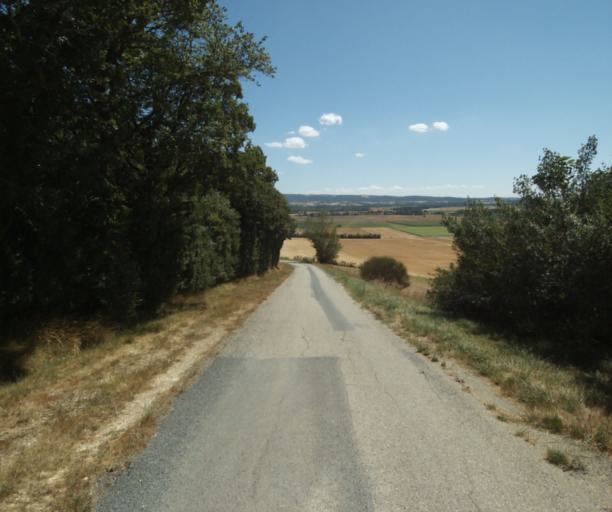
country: FR
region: Midi-Pyrenees
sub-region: Departement de la Haute-Garonne
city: Saint-Felix-Lauragais
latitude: 43.4609
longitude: 1.9203
